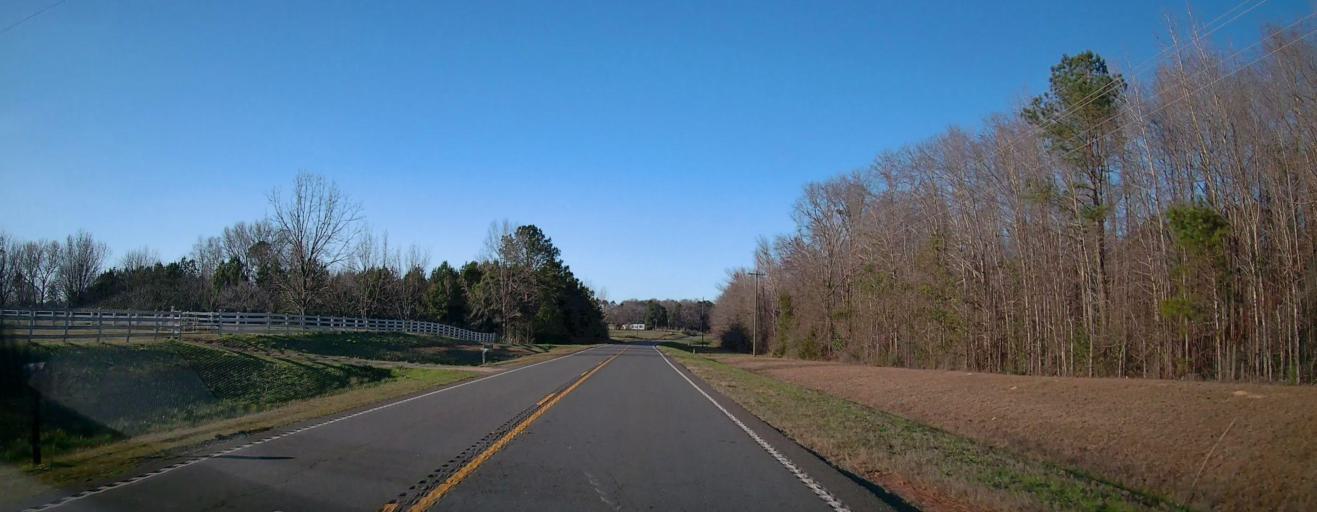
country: US
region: Georgia
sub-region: Talbot County
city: Talbotton
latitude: 32.5941
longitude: -84.5556
